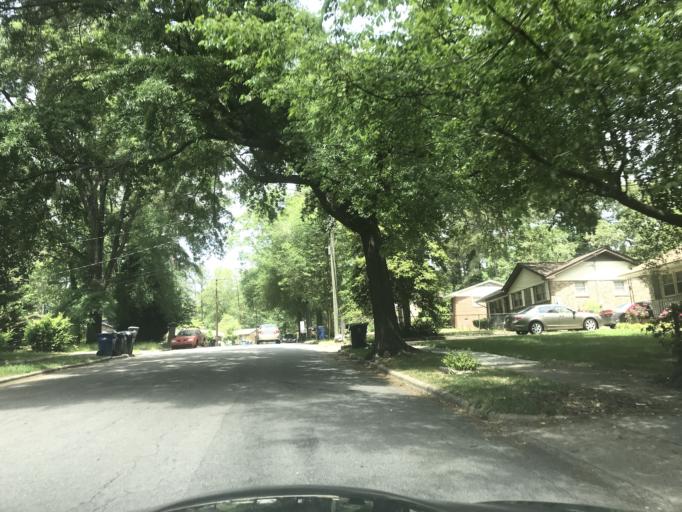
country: US
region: North Carolina
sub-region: Wake County
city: Raleigh
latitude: 35.7674
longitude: -78.5862
